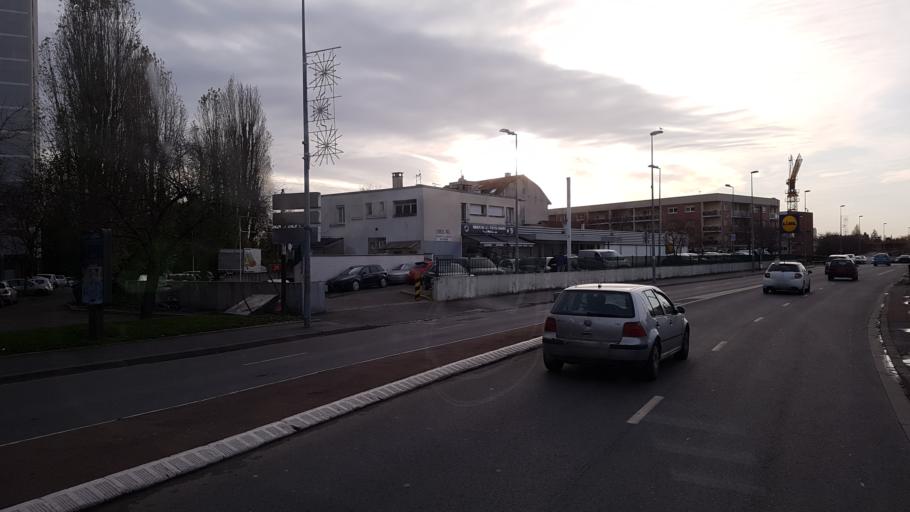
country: FR
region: Ile-de-France
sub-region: Departement de Seine-Saint-Denis
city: Le Blanc-Mesnil
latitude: 48.9274
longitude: 2.4736
